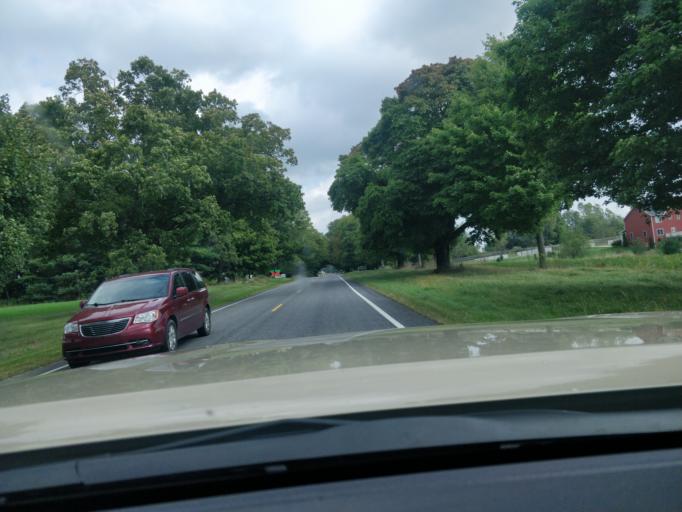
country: US
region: Michigan
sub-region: Kent County
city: Lowell
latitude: 42.8860
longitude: -85.3047
